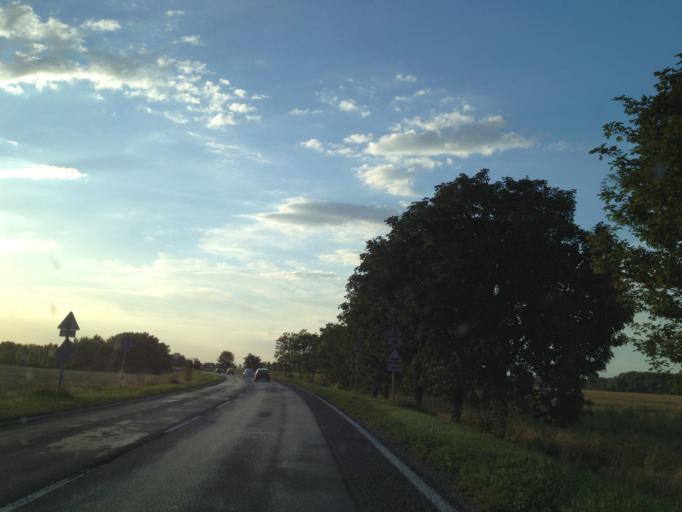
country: HU
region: Gyor-Moson-Sopron
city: Lebeny
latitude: 47.7791
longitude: 17.4173
